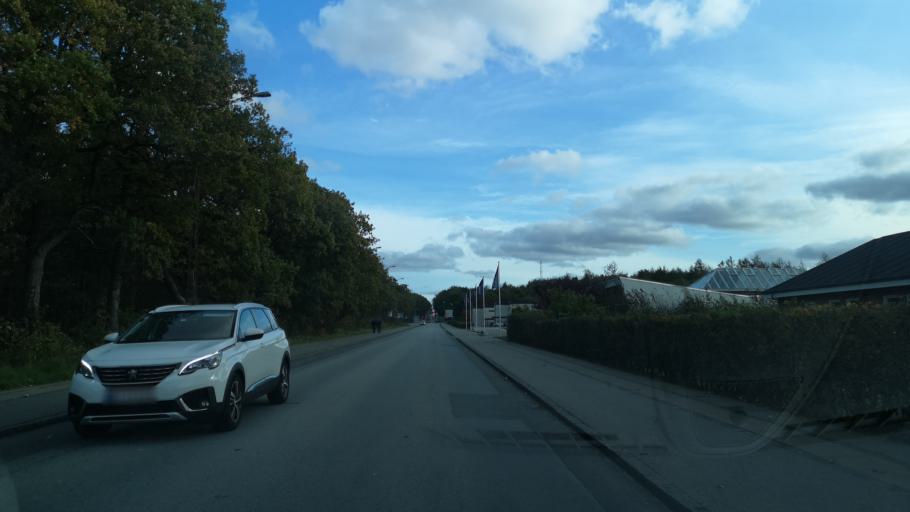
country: DK
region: Central Jutland
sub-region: Holstebro Kommune
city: Holstebro
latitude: 56.3480
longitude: 8.6279
